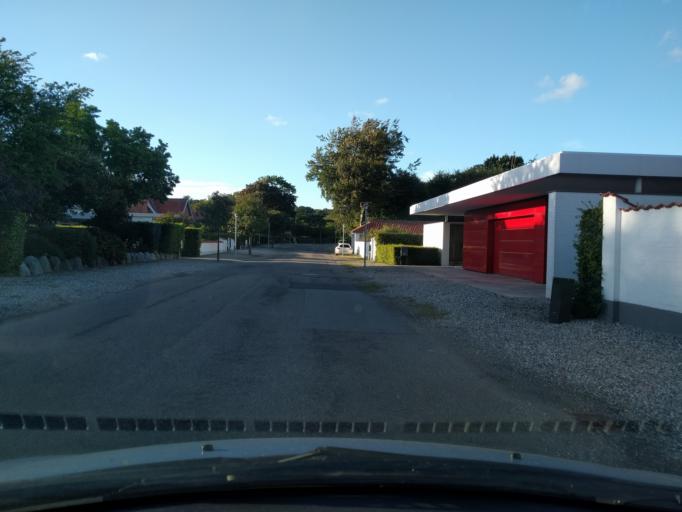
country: DK
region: South Denmark
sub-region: Nyborg Kommune
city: Nyborg
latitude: 55.3286
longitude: 10.8078
